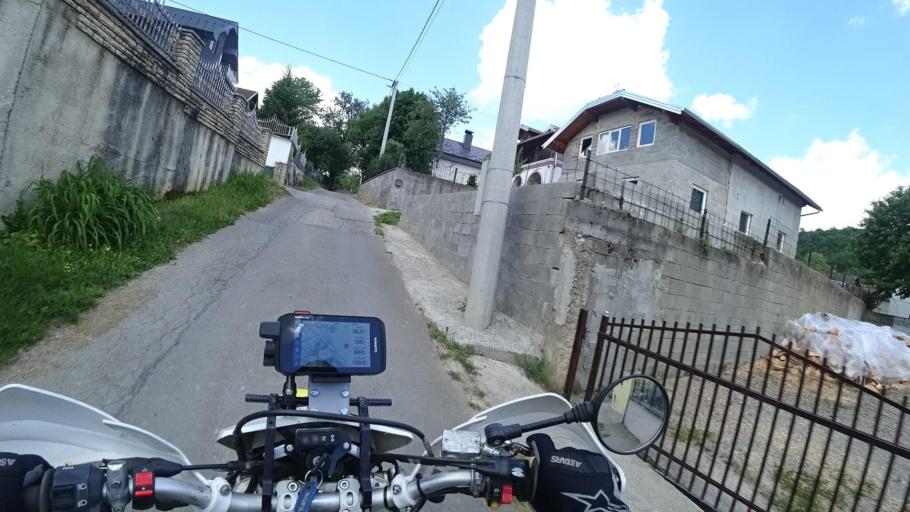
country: BA
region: Federation of Bosnia and Herzegovina
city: Bihac
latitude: 44.8183
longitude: 15.9142
